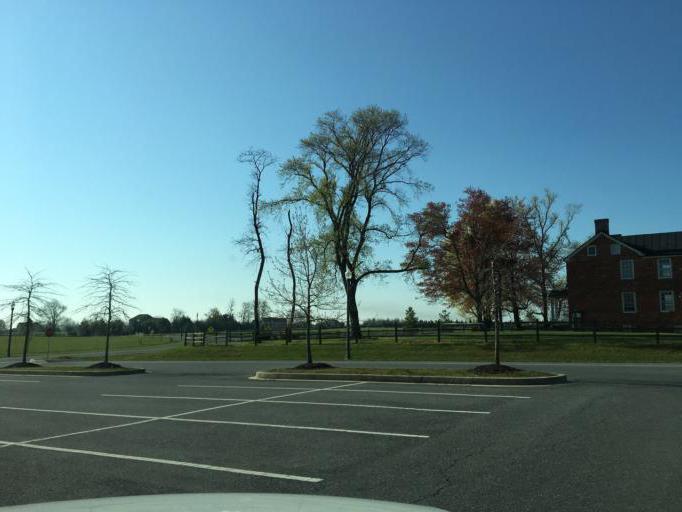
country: US
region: Maryland
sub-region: Frederick County
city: Walkersville
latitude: 39.5162
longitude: -77.4022
